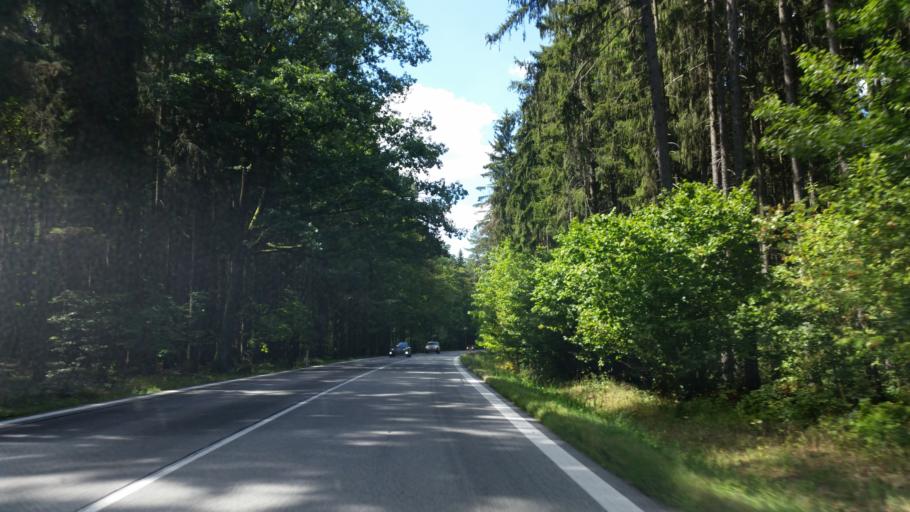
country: CZ
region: Vysocina
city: Cernovice
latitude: 49.4213
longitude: 14.9700
